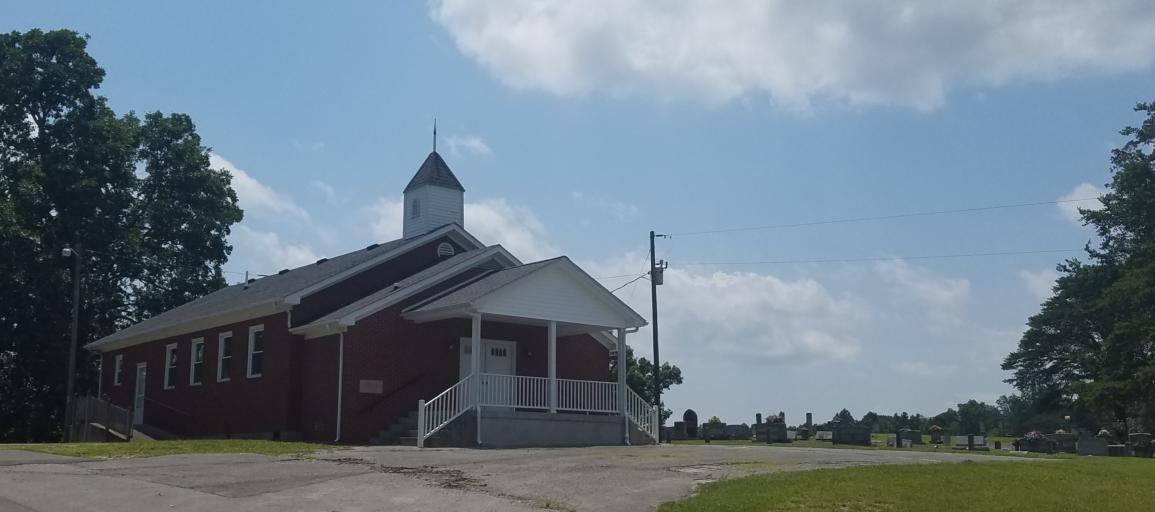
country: US
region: Kentucky
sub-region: Hart County
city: Munfordville
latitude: 37.3061
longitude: -86.0628
